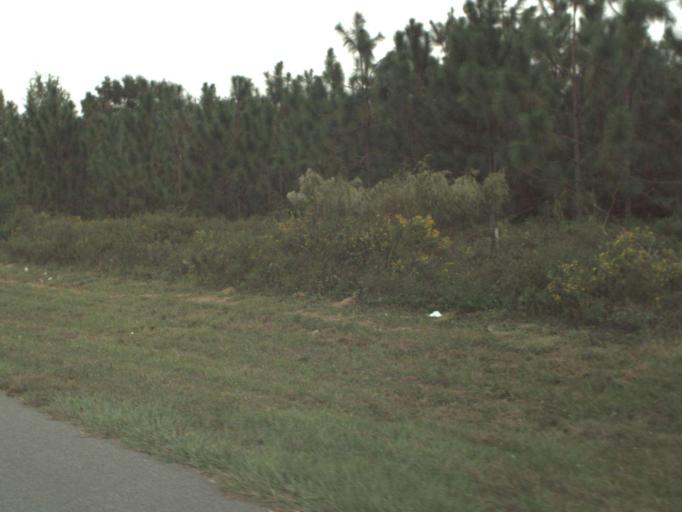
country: US
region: Florida
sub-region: Jackson County
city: Sneads
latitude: 30.7475
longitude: -85.0195
